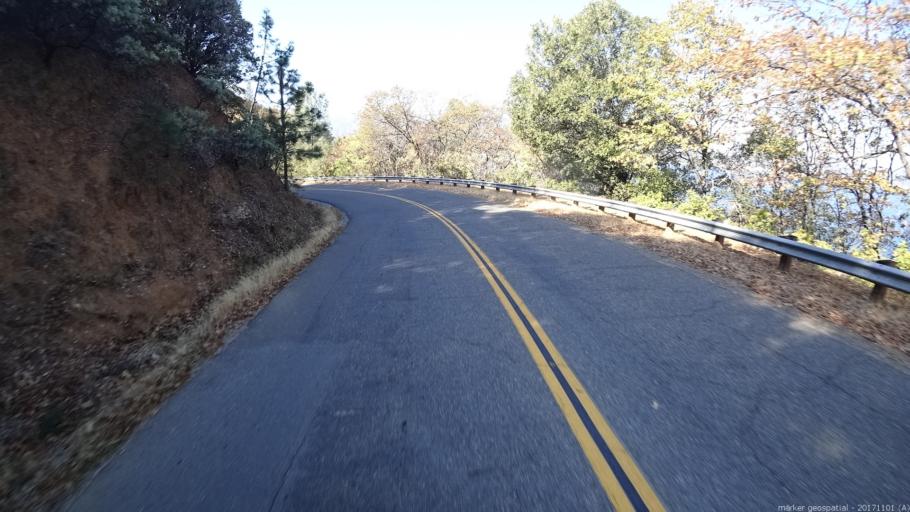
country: US
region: California
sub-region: Shasta County
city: Central Valley (historical)
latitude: 40.7142
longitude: -122.4120
